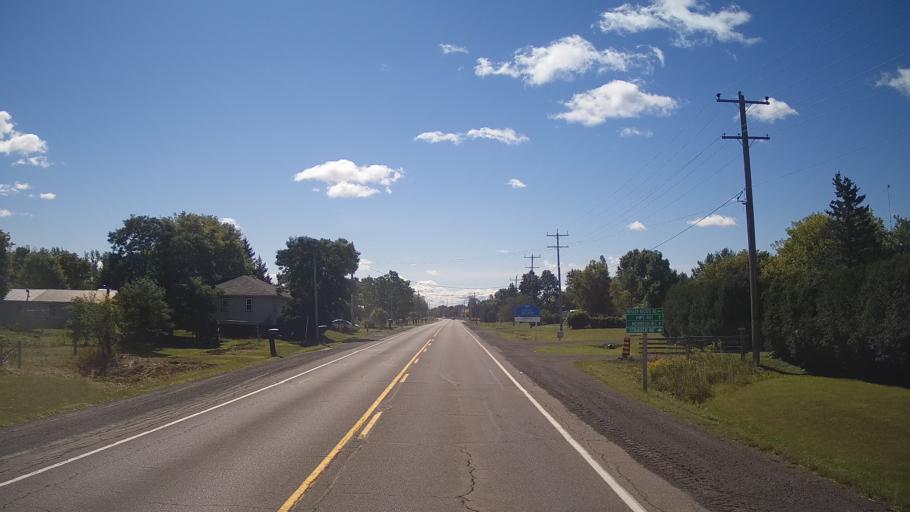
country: US
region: New York
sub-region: St. Lawrence County
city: Norfolk
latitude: 44.9386
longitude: -75.2150
